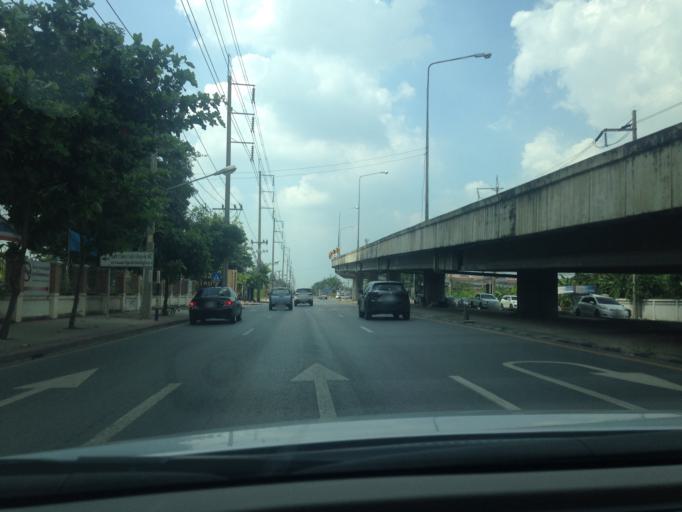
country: TH
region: Phra Nakhon Si Ayutthaya
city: Ban Bang Kadi Pathum Thani
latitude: 14.0133
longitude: 100.5514
